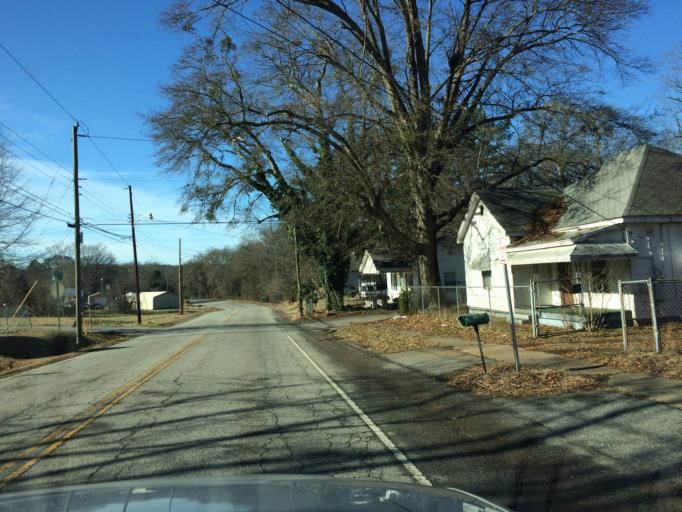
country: US
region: South Carolina
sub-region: Spartanburg County
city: Arcadia
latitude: 34.9603
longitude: -81.9920
